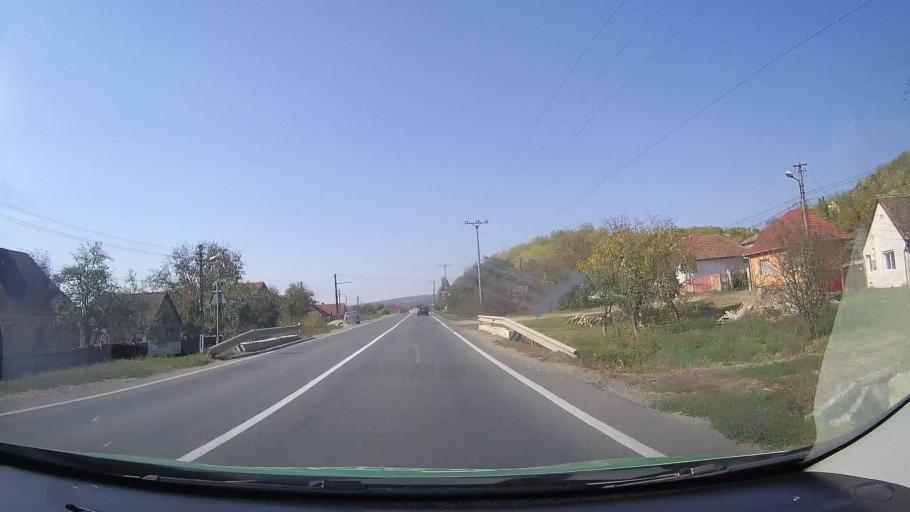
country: RO
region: Arad
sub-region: Oras Lipova
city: Radna
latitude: 46.0971
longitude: 21.6775
